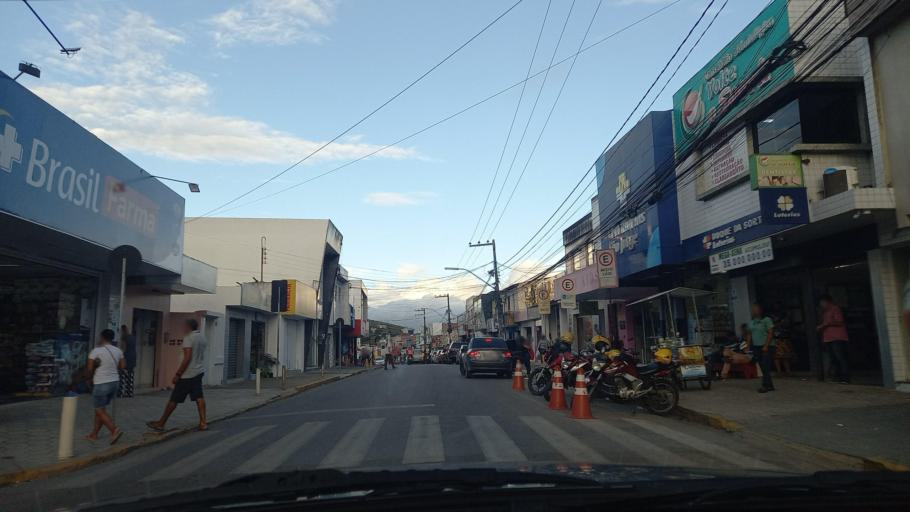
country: BR
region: Pernambuco
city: Garanhuns
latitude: -8.8848
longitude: -36.4688
